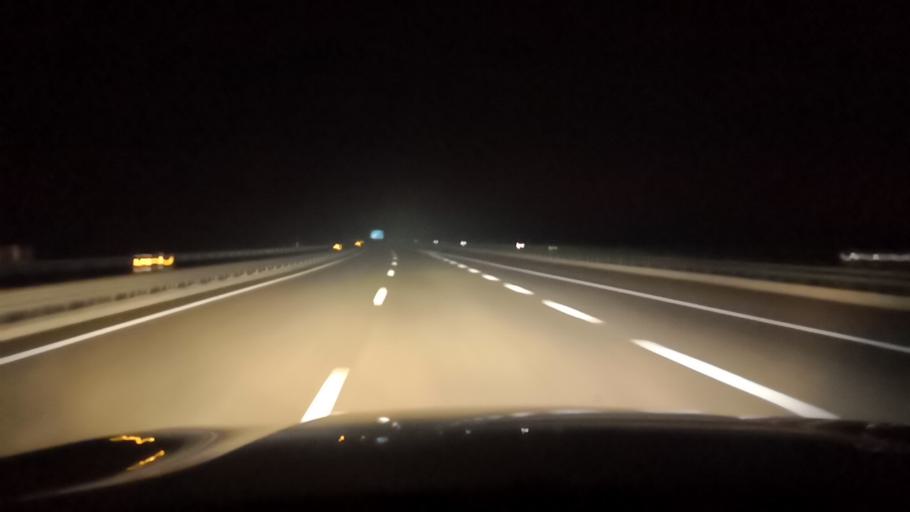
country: PT
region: Santarem
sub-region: Benavente
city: Poceirao
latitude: 38.8917
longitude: -8.7913
